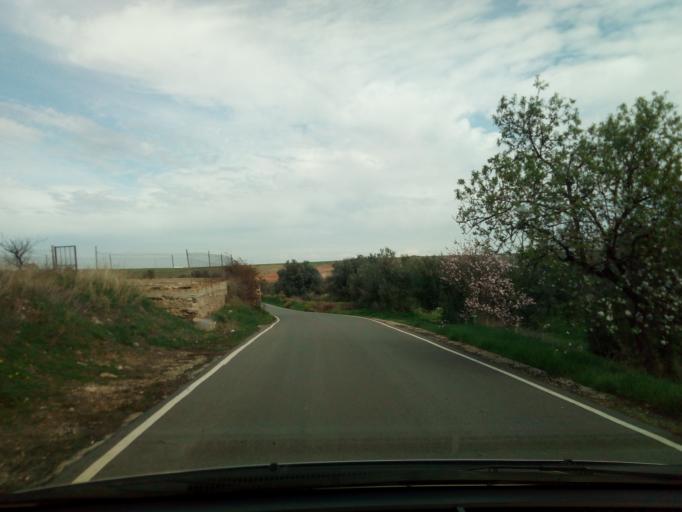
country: CY
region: Lefkosia
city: Astromeritis
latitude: 35.0876
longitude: 32.9949
